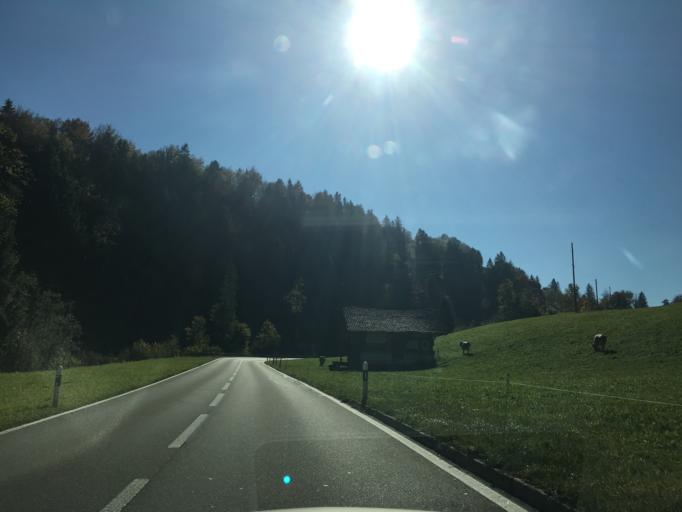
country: CH
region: Bern
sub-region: Obersimmental-Saanen District
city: Boltigen
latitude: 46.6571
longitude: 7.4444
